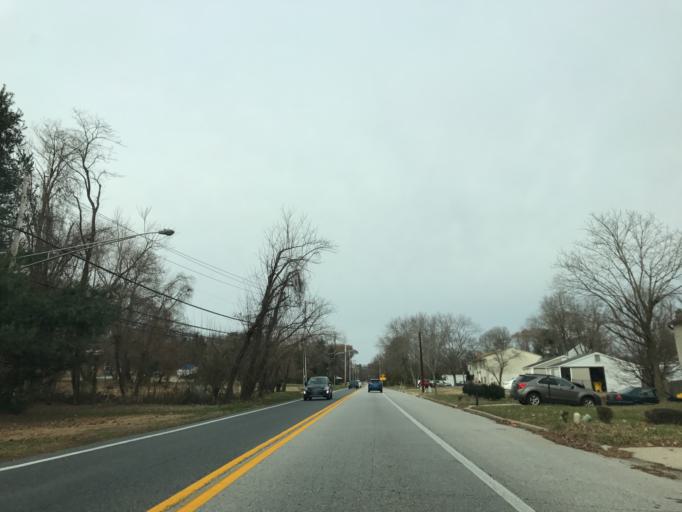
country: US
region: Maryland
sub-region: Anne Arundel County
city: Pasadena
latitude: 39.0968
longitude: -76.5489
